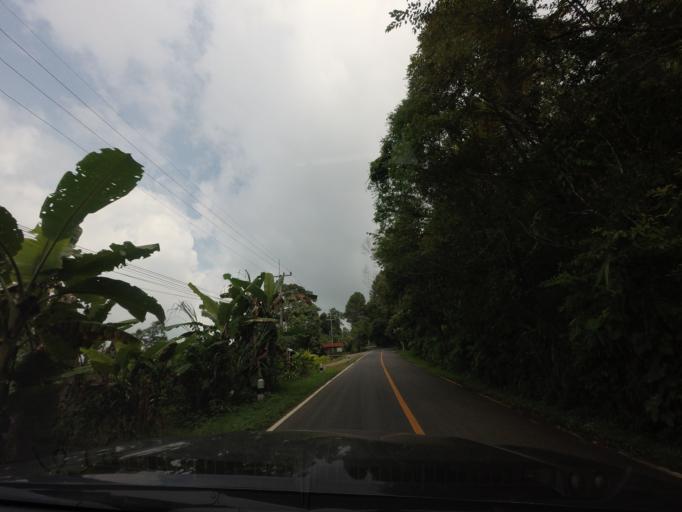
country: TH
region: Nan
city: Pua
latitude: 19.1884
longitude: 101.0237
